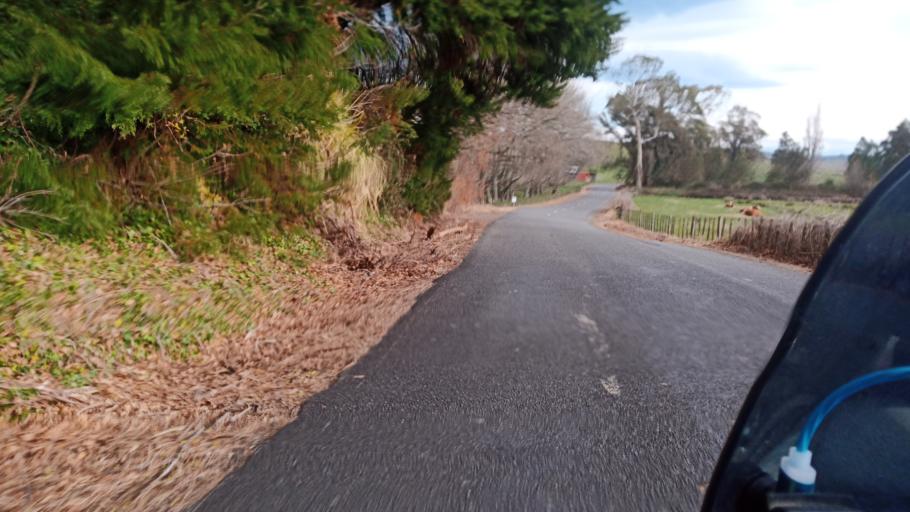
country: NZ
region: Hawke's Bay
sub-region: Wairoa District
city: Wairoa
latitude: -38.9750
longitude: 177.4260
